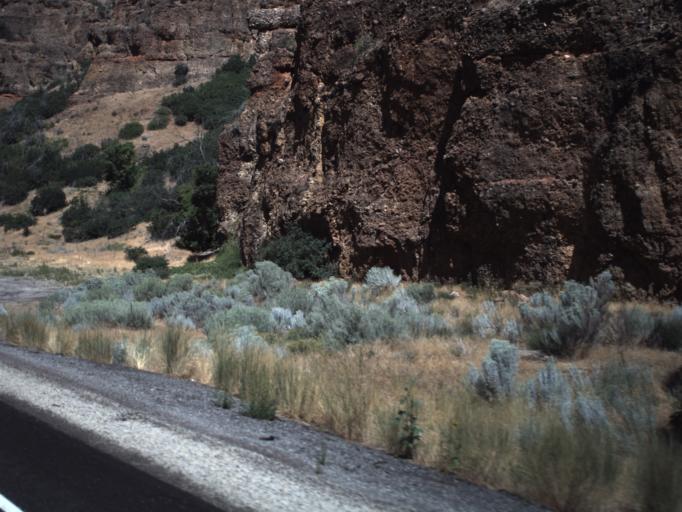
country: US
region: Utah
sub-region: Utah County
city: Mapleton
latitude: 39.9930
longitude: -111.3983
